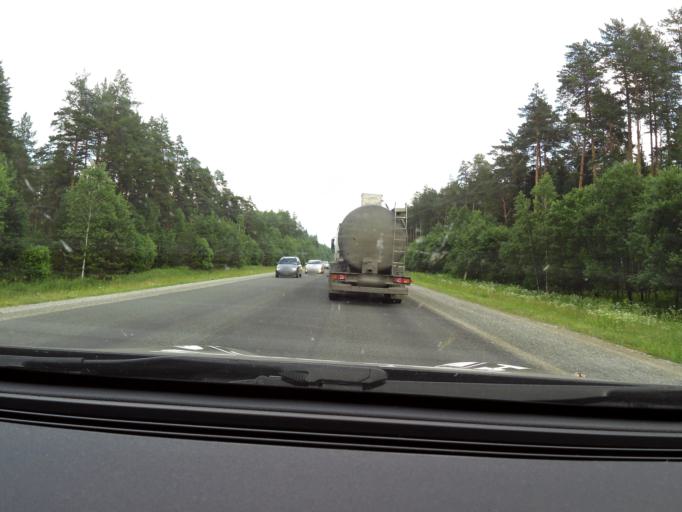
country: RU
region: Sverdlovsk
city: Achit
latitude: 56.7805
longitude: 57.9584
